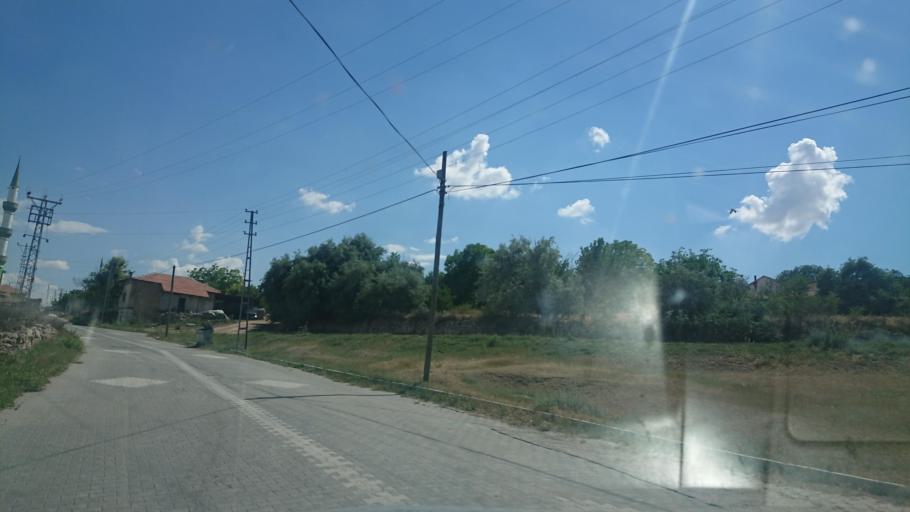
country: TR
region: Aksaray
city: Agacoren
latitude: 38.7727
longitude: 33.7853
